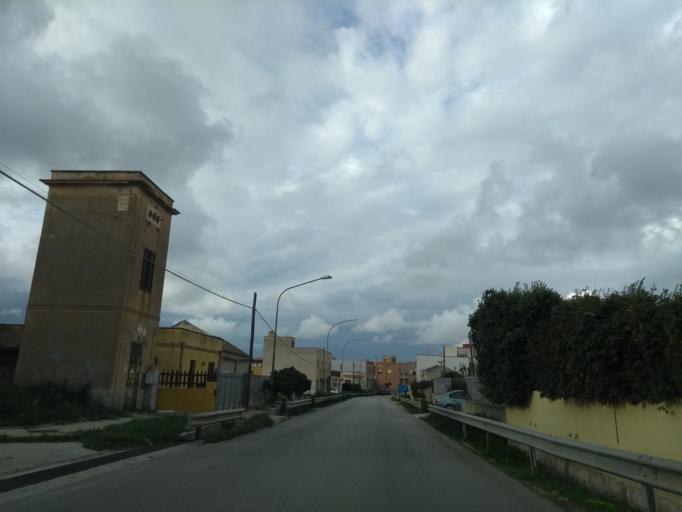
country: IT
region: Sicily
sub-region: Trapani
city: Marausa
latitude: 37.9640
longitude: 12.5185
